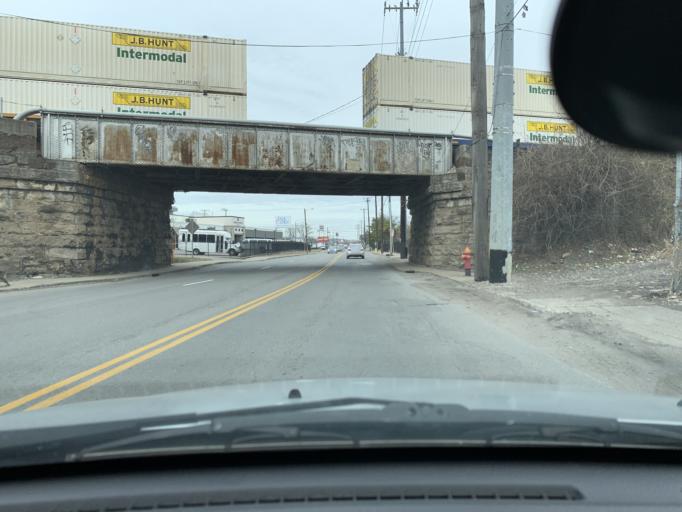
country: US
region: Tennessee
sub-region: Davidson County
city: Nashville
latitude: 36.1730
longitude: -86.7739
